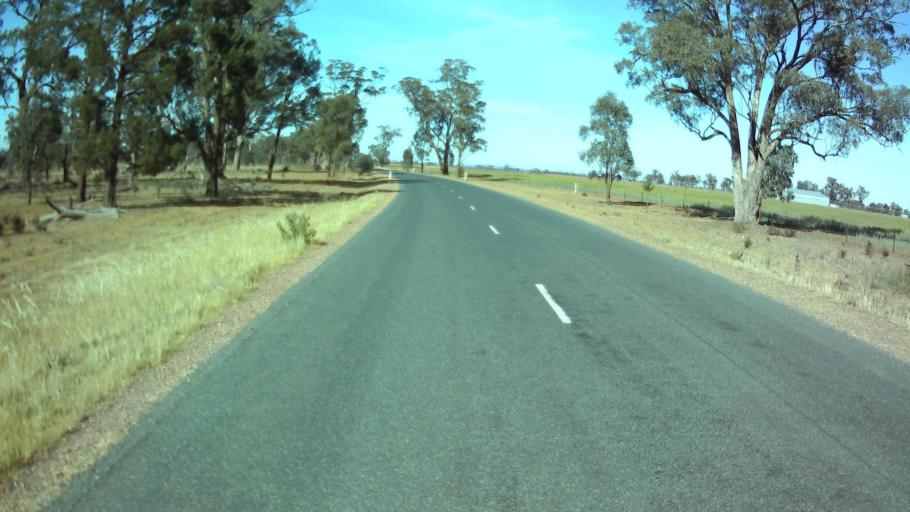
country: AU
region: New South Wales
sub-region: Weddin
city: Grenfell
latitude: -34.1151
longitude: 147.8207
